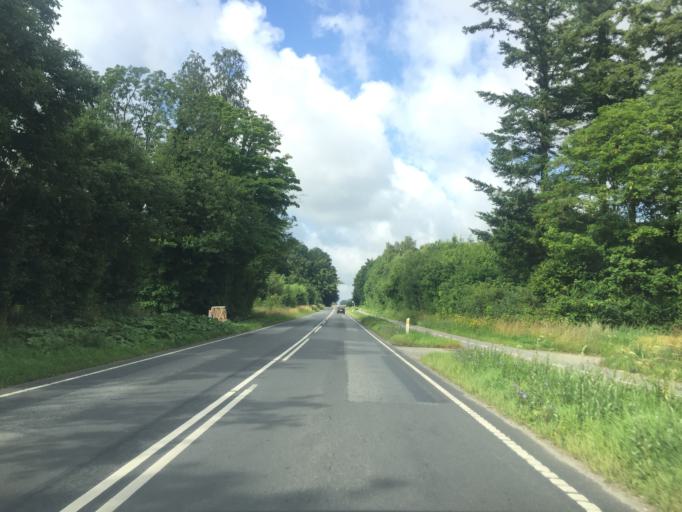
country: DK
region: South Denmark
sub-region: Svendborg Kommune
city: Thuro By
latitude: 55.0827
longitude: 10.6773
